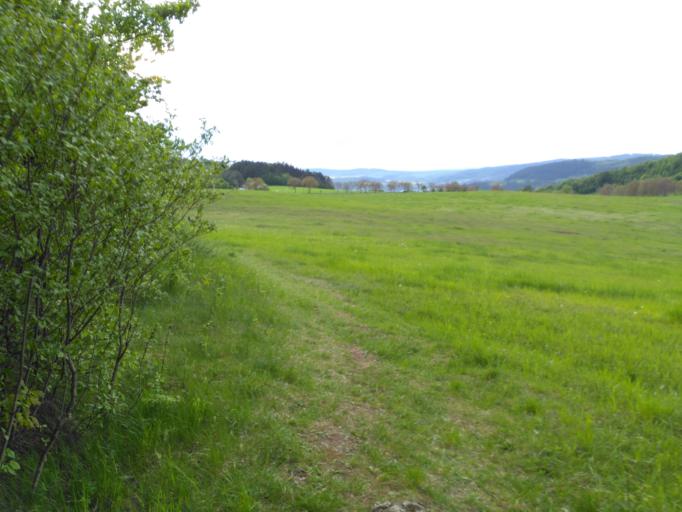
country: CZ
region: Central Bohemia
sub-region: Okres Beroun
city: Beroun
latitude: 49.9144
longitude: 14.0787
